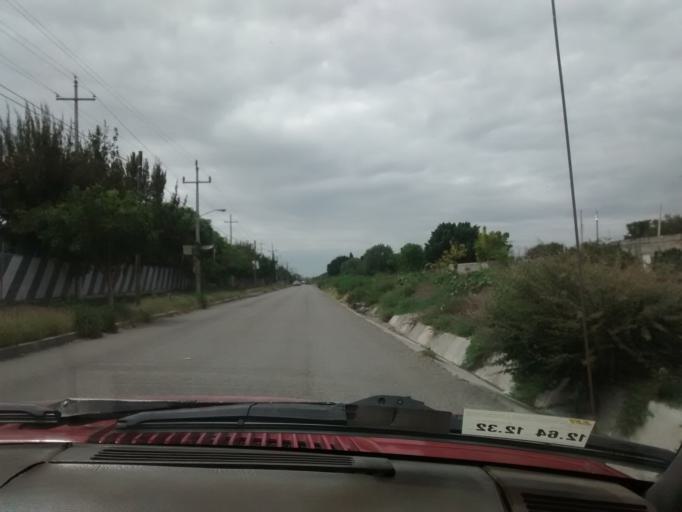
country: MX
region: Puebla
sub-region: Santiago Miahuatlan
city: San Jose Monte Chiquito
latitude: 18.4920
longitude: -97.4194
